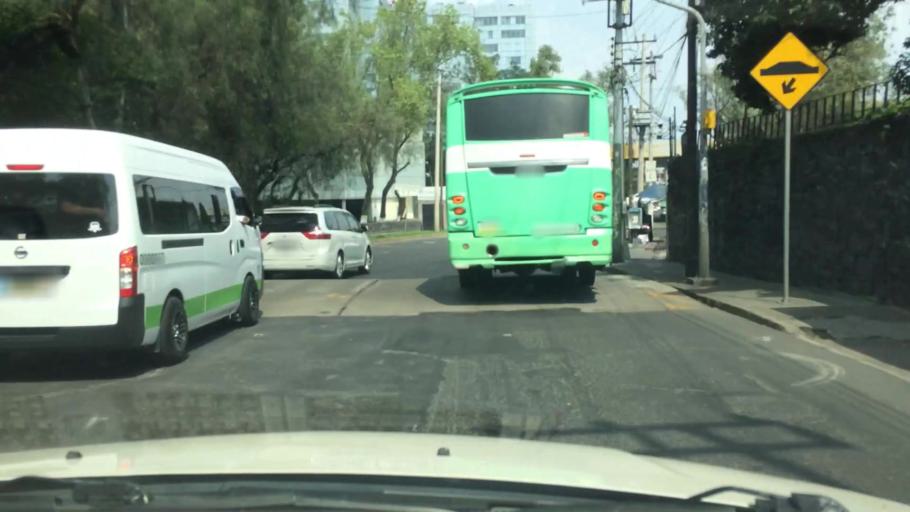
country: MX
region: Mexico City
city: Magdalena Contreras
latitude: 19.3368
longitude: -99.1918
